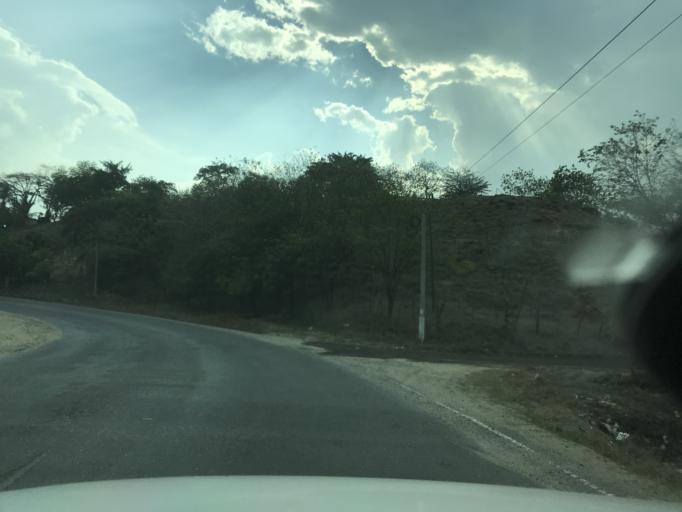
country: GT
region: Zacapa
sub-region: Municipio de Zacapa
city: Gualan
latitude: 15.1816
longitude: -89.3020
